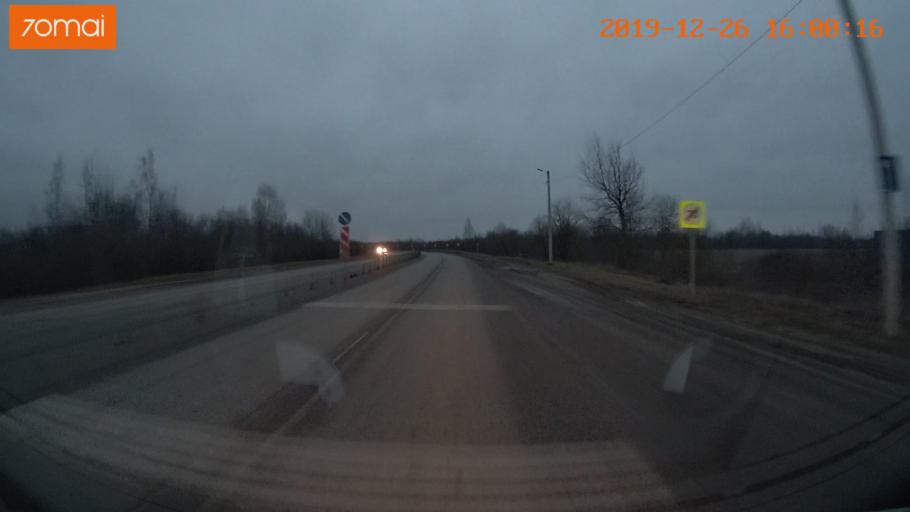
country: RU
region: Jaroslavl
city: Rybinsk
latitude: 58.0260
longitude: 38.8035
